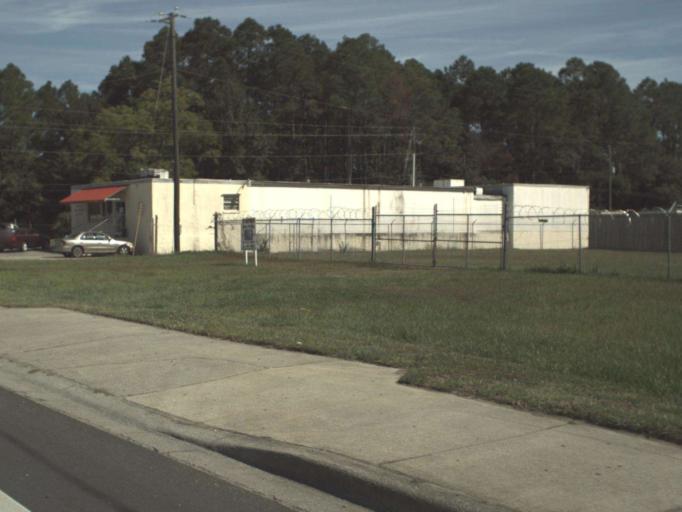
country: US
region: Florida
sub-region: Bay County
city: Panama City
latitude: 30.1779
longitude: -85.6501
